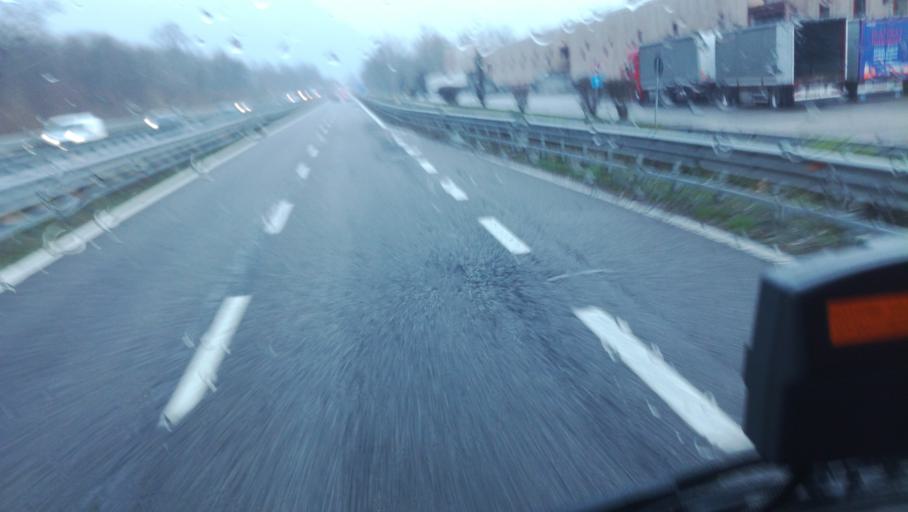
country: IT
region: Lombardy
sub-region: Provincia di Lecco
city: Molteno
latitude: 45.7887
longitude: 9.2974
